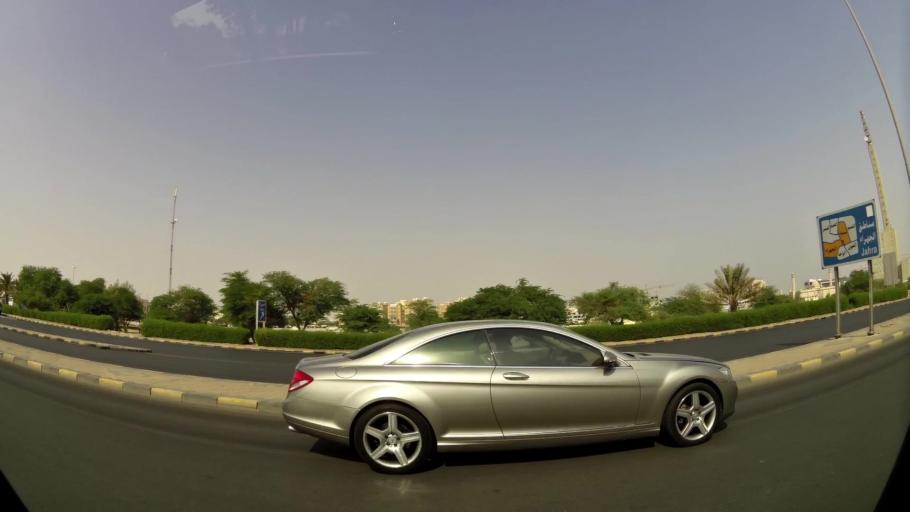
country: KW
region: Muhafazat al Jahra'
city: Al Jahra'
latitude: 29.3355
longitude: 47.6674
